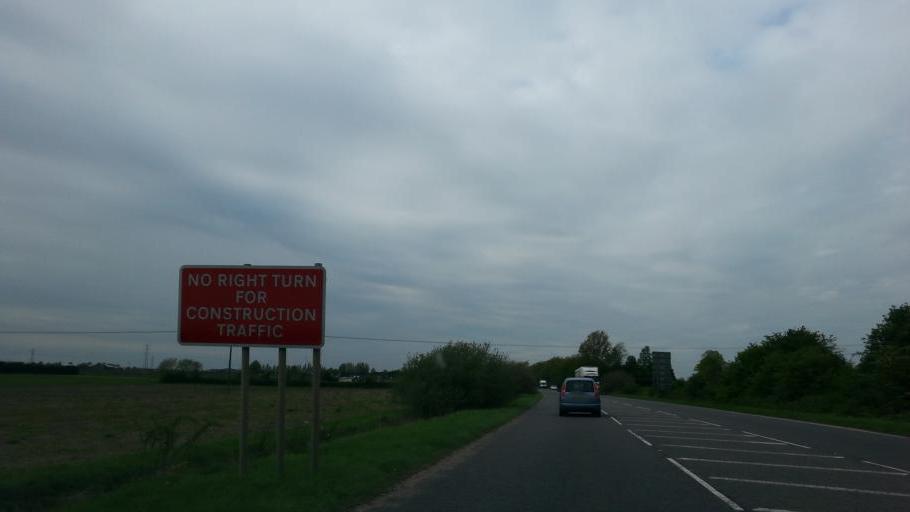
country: GB
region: England
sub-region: Cambridgeshire
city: March
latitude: 52.5457
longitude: 0.0706
